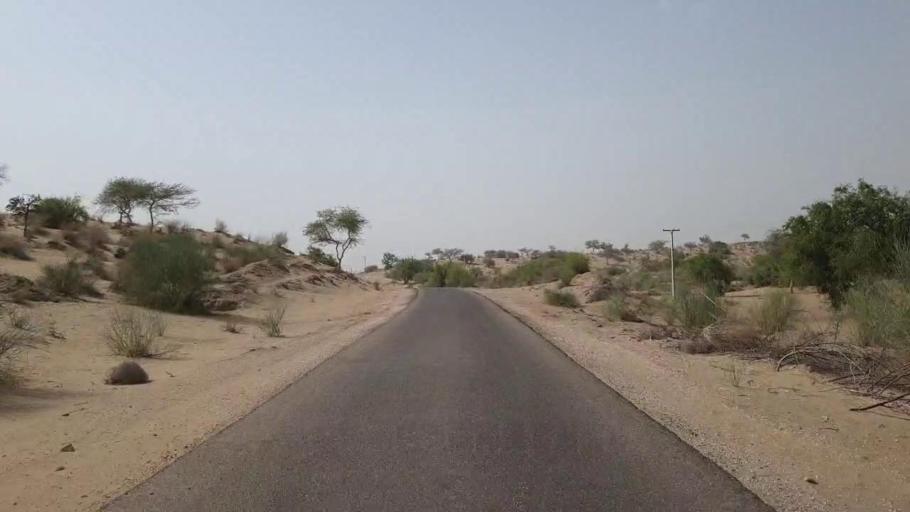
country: PK
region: Sindh
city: Mithi
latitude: 24.5960
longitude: 69.9249
